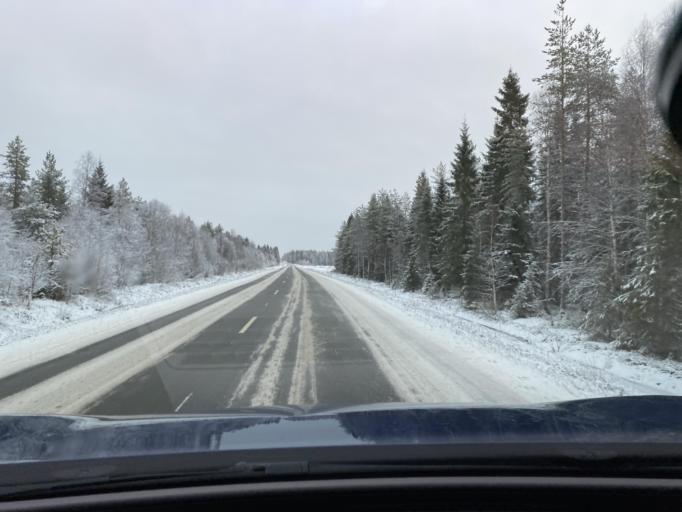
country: FI
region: Lapland
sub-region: Rovaniemi
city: Ranua
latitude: 65.9844
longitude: 26.1580
